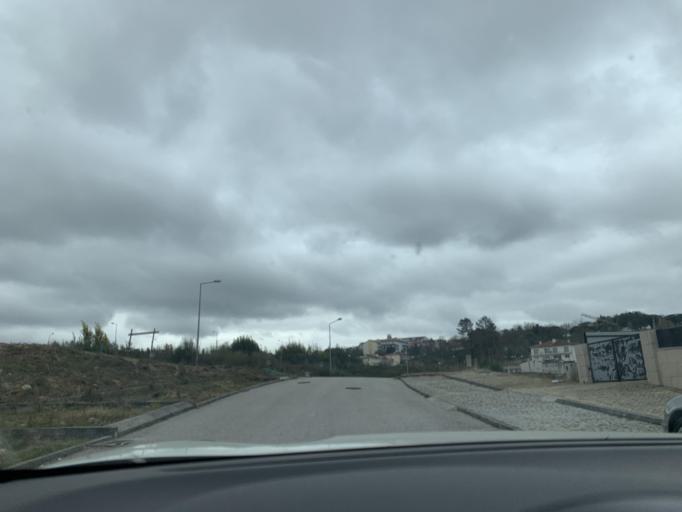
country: PT
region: Viseu
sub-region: Mangualde
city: Mangualde
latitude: 40.6108
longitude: -7.7693
